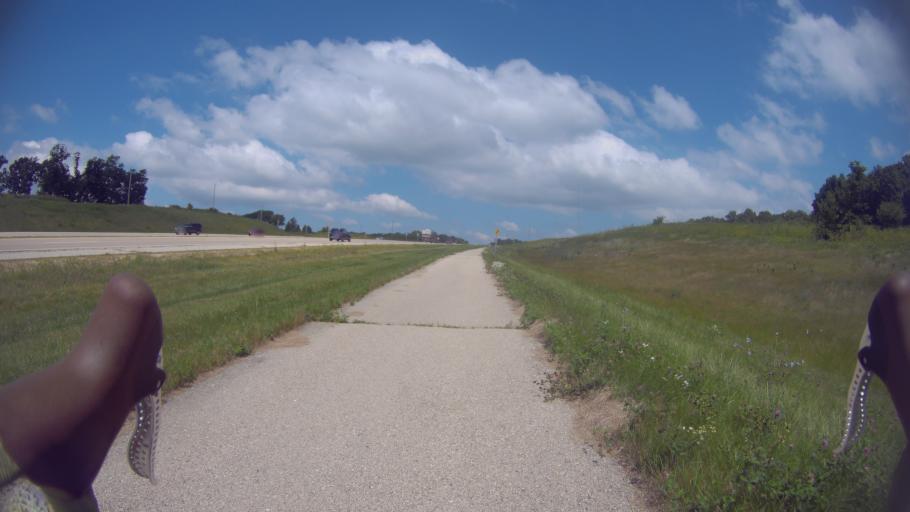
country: US
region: Wisconsin
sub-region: Dane County
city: Cross Plains
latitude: 43.2044
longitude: -89.5932
